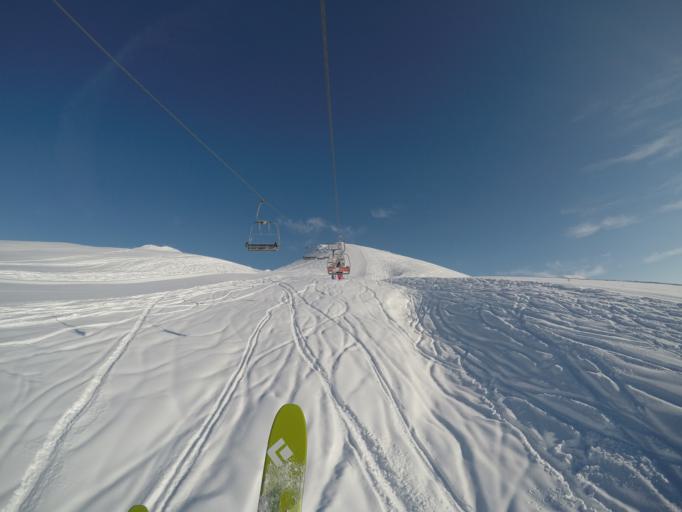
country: GE
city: Gudauri
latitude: 42.4912
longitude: 44.5016
